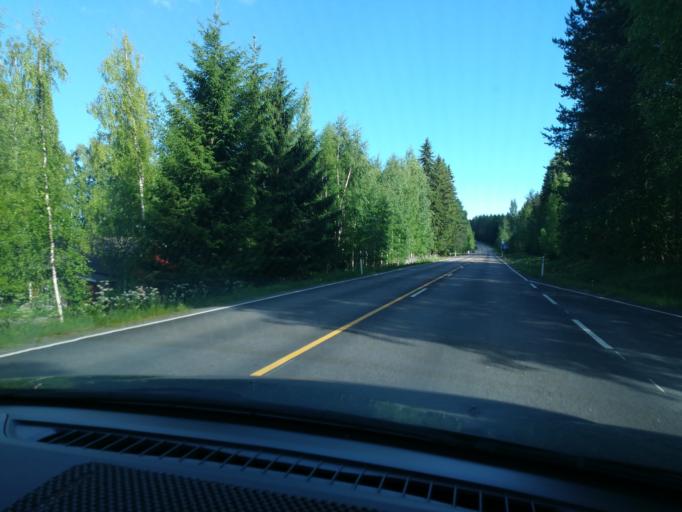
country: FI
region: Southern Savonia
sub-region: Mikkeli
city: Puumala
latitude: 61.5104
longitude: 28.1822
